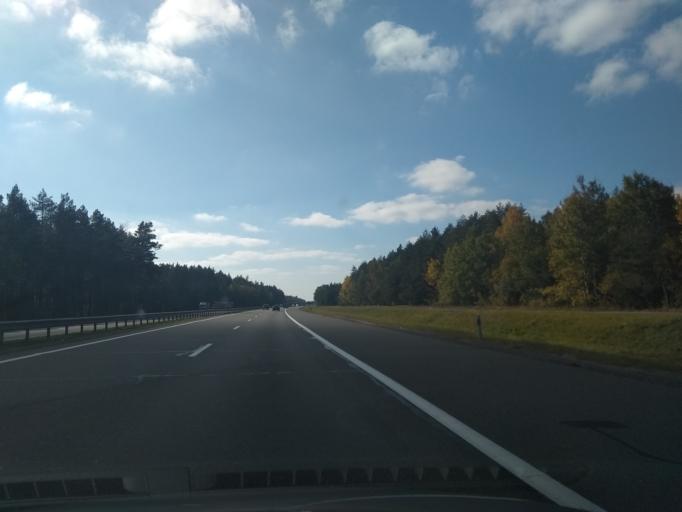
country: BY
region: Brest
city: Baranovichi
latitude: 53.0543
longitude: 25.8579
